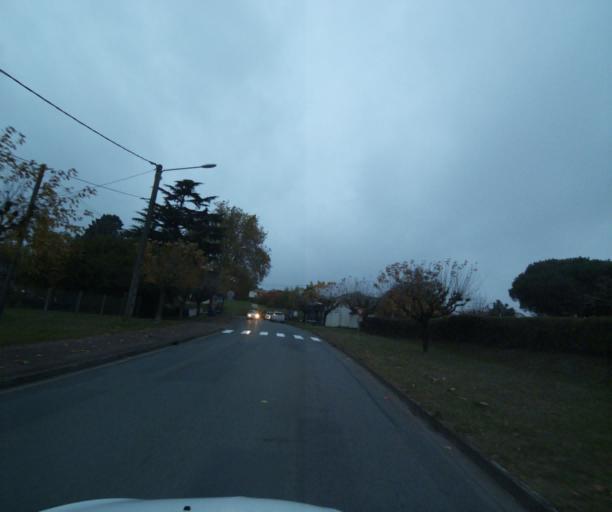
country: FR
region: Poitou-Charentes
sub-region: Departement de la Charente-Maritime
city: Fontcouverte
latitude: 45.7453
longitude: -0.6047
